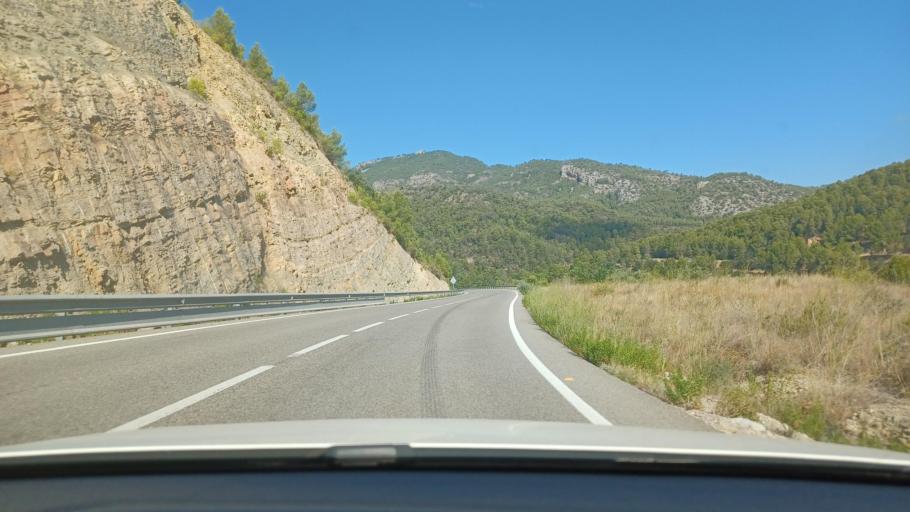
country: ES
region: Catalonia
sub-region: Provincia de Tarragona
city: Benifallet
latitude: 40.9510
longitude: 0.4519
